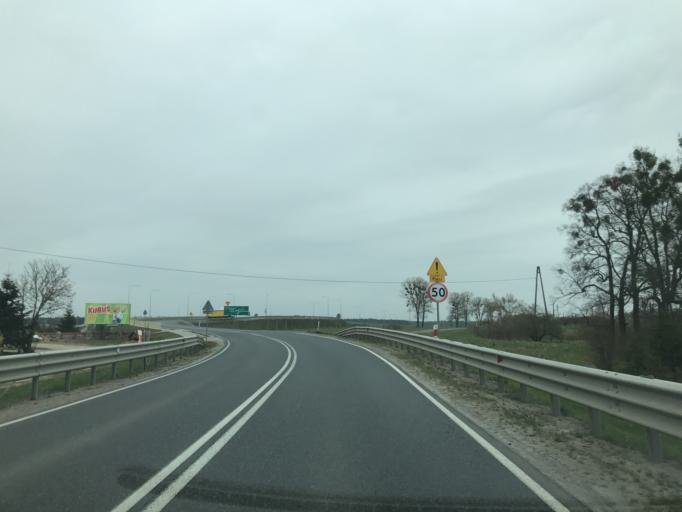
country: PL
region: Warmian-Masurian Voivodeship
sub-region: Powiat olsztynski
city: Olsztynek
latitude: 53.6005
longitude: 20.3048
